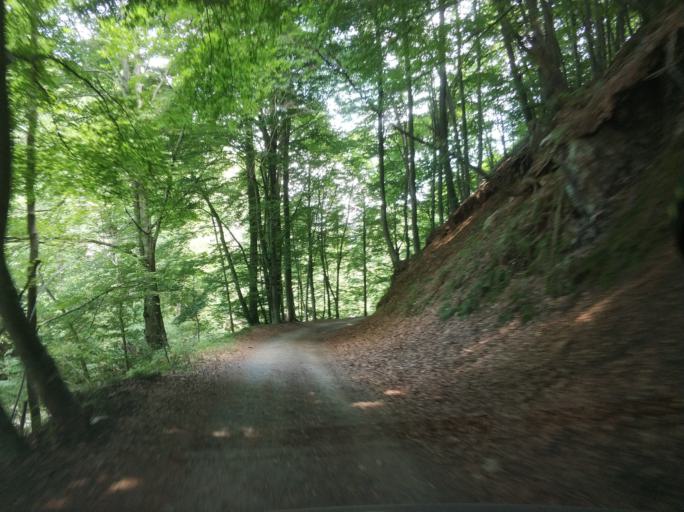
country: IT
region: Piedmont
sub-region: Provincia di Torino
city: Viu
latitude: 45.2004
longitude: 7.3926
